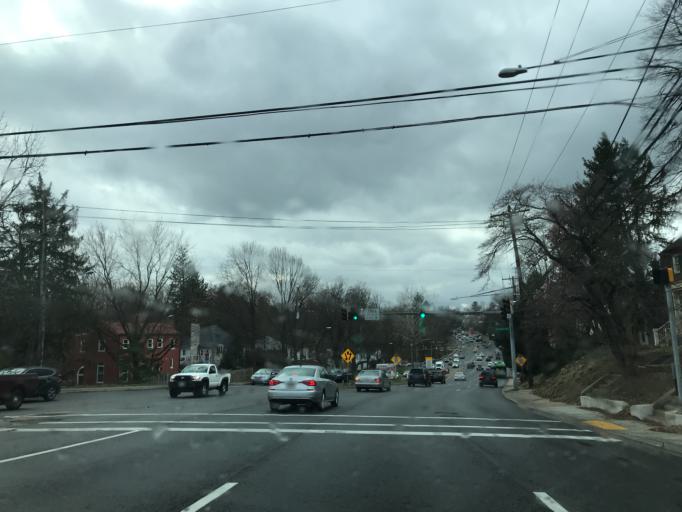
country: US
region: Maryland
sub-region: Montgomery County
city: Four Corners
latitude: 39.0092
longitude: -77.0181
